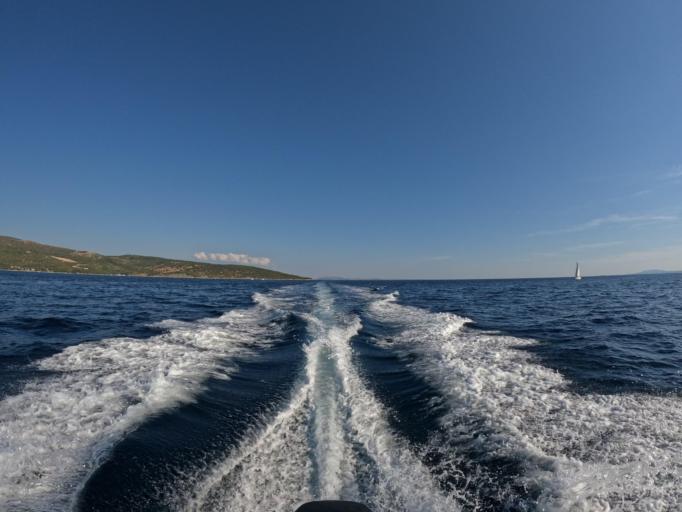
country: HR
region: Primorsko-Goranska
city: Punat
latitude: 44.9964
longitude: 14.6013
